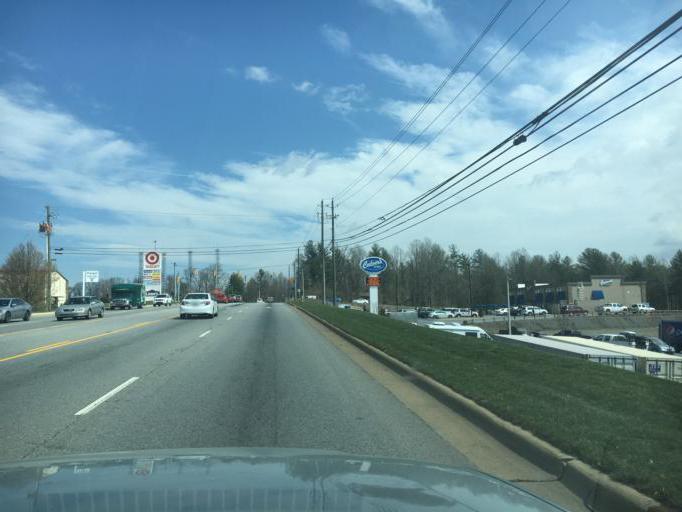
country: US
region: North Carolina
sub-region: Buncombe County
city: Royal Pines
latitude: 35.4456
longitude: -82.5332
